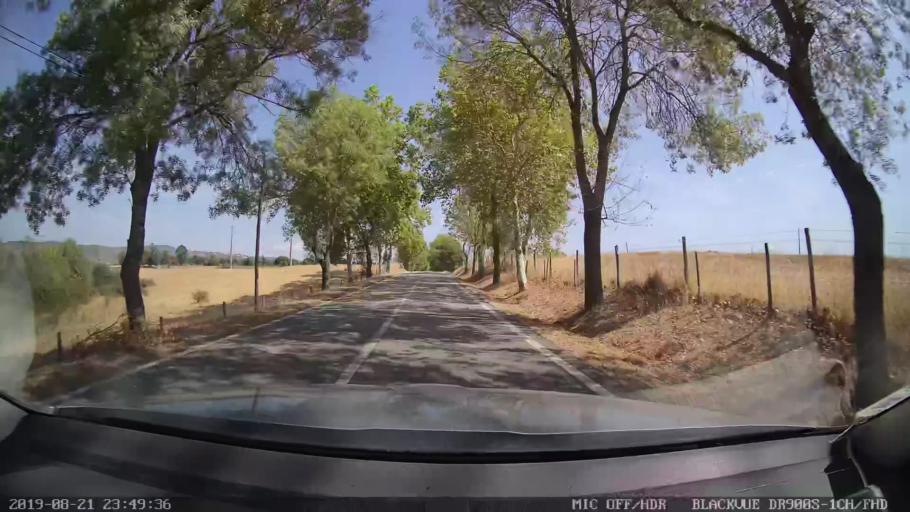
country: PT
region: Castelo Branco
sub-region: Idanha-A-Nova
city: Idanha-a-Nova
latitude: 39.8796
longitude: -7.2488
